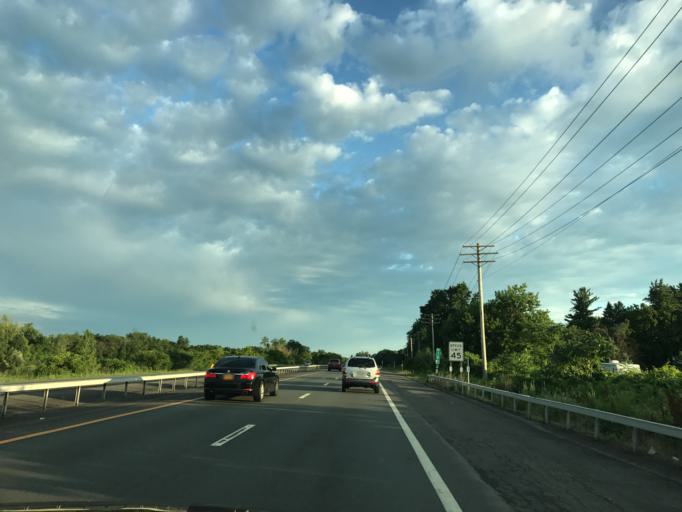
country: US
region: New York
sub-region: Albany County
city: Green Island
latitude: 42.7581
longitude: -73.6984
